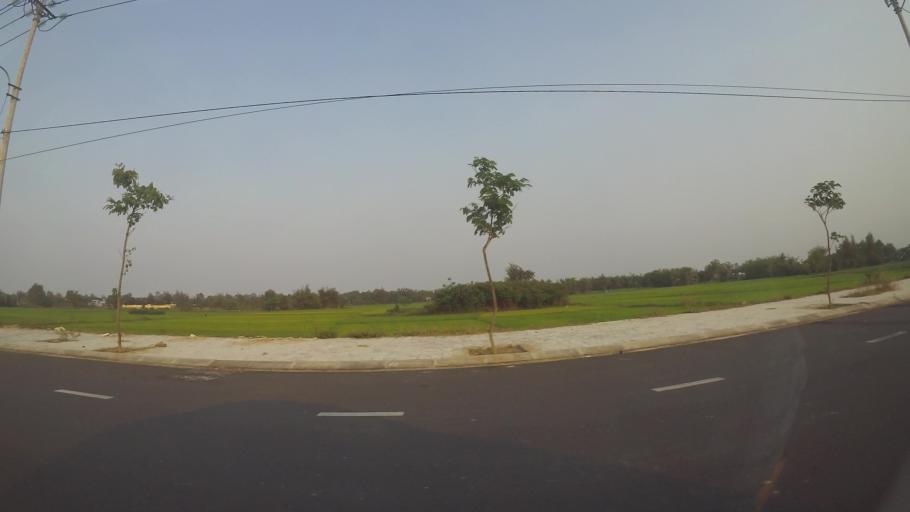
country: VN
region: Da Nang
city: Ngu Hanh Son
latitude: 15.9746
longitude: 108.2326
